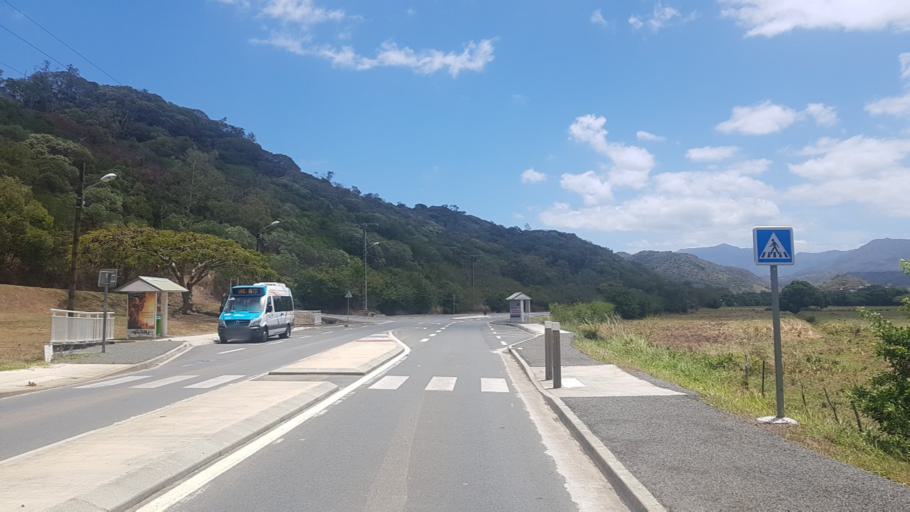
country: NC
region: South Province
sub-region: Dumbea
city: Dumbea
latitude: -22.1667
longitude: 166.4567
